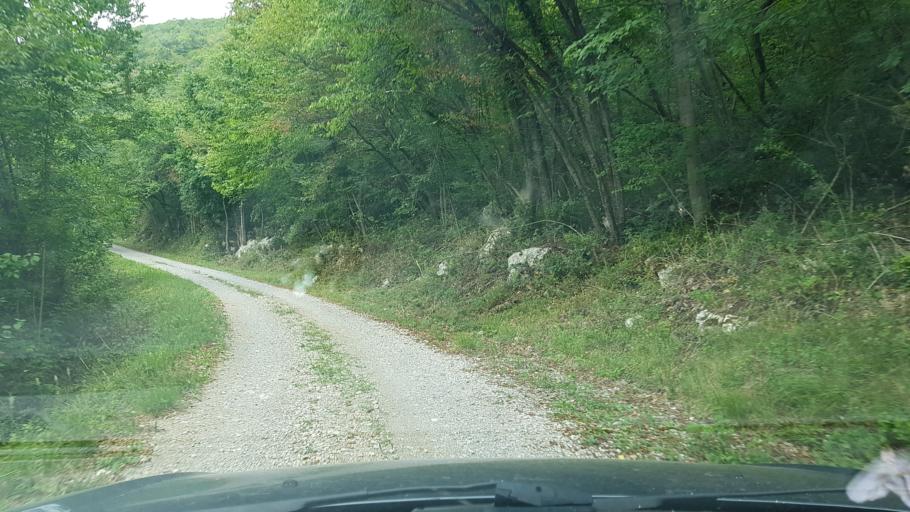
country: SI
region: Kanal
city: Deskle
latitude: 46.0159
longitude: 13.6266
